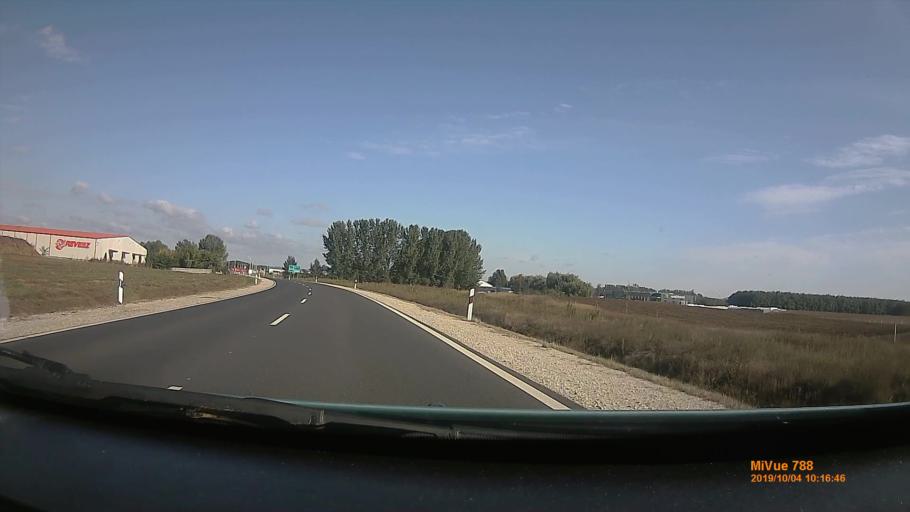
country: HU
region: Szabolcs-Szatmar-Bereg
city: Nyiregyhaza
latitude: 47.9525
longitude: 21.6552
